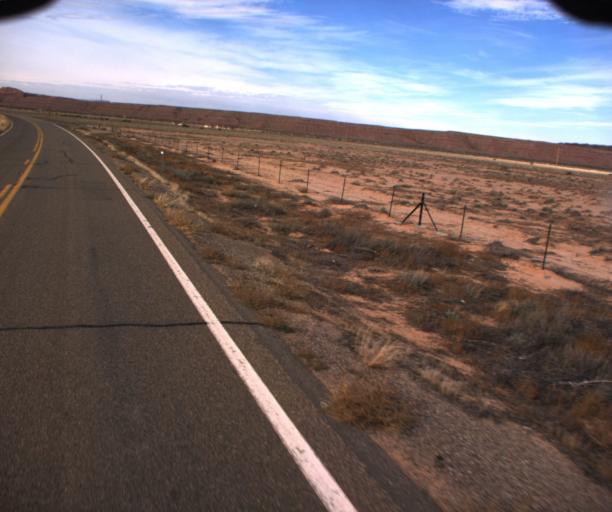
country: US
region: Arizona
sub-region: Apache County
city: Many Farms
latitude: 36.4644
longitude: -109.5975
